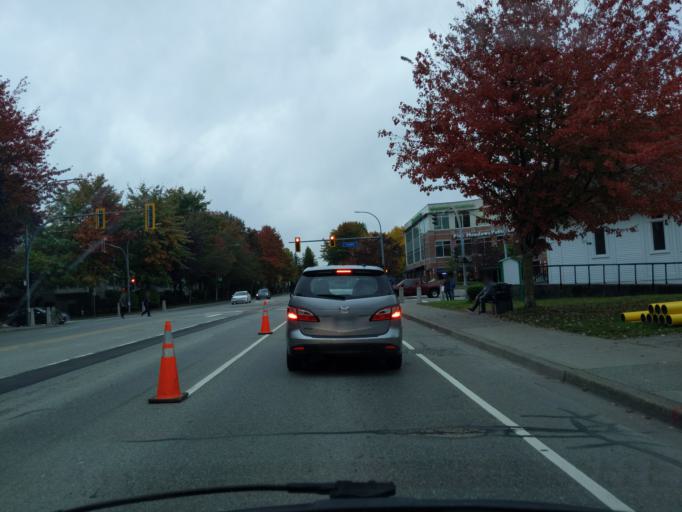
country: CA
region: British Columbia
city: Pitt Meadows
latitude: 49.2229
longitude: -122.6897
